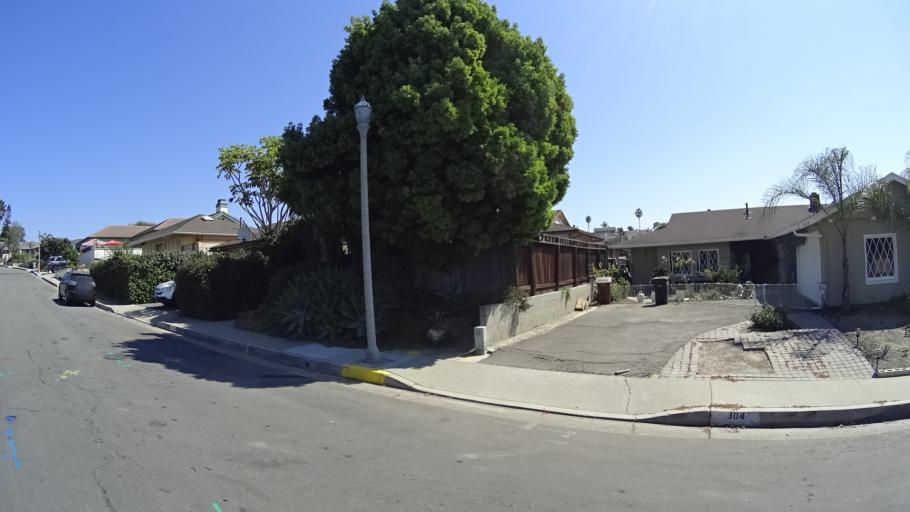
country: US
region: California
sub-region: Orange County
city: San Clemente
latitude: 33.4446
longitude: -117.6389
